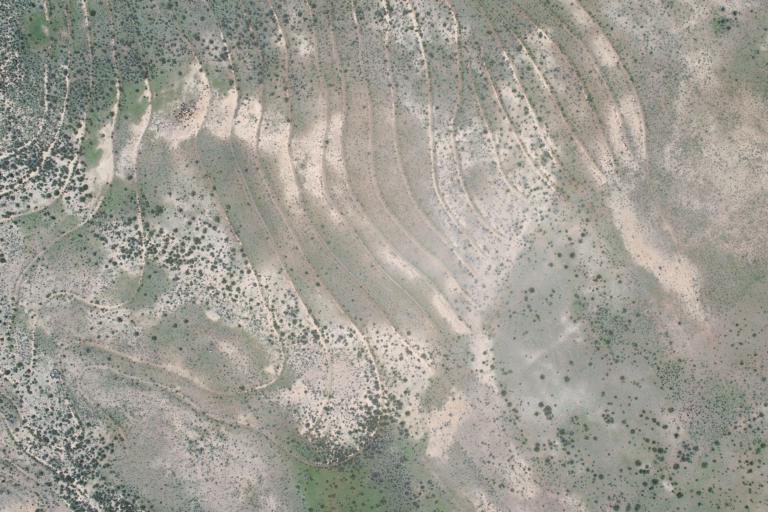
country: BO
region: La Paz
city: Curahuara de Carangas
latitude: -17.2838
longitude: -68.5095
